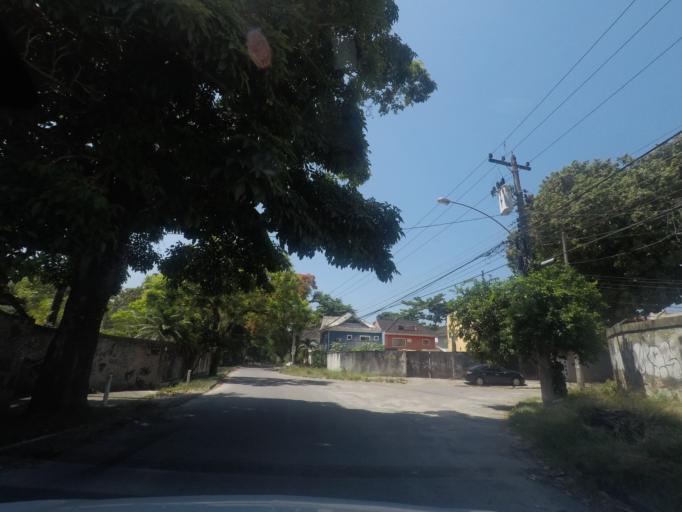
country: BR
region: Rio de Janeiro
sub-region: Nilopolis
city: Nilopolis
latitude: -22.9817
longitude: -43.4594
